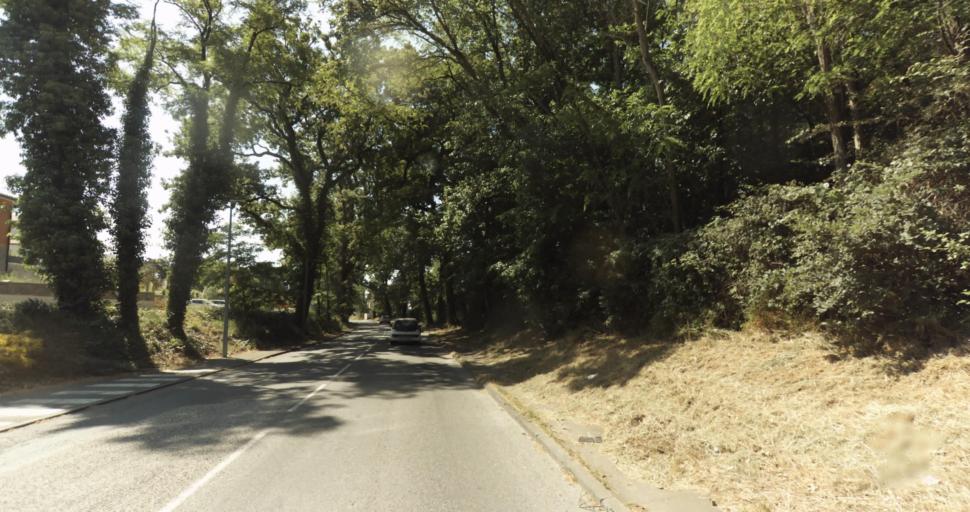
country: FR
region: Midi-Pyrenees
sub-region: Departement de la Haute-Garonne
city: Plaisance-du-Touch
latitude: 43.5739
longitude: 1.2917
